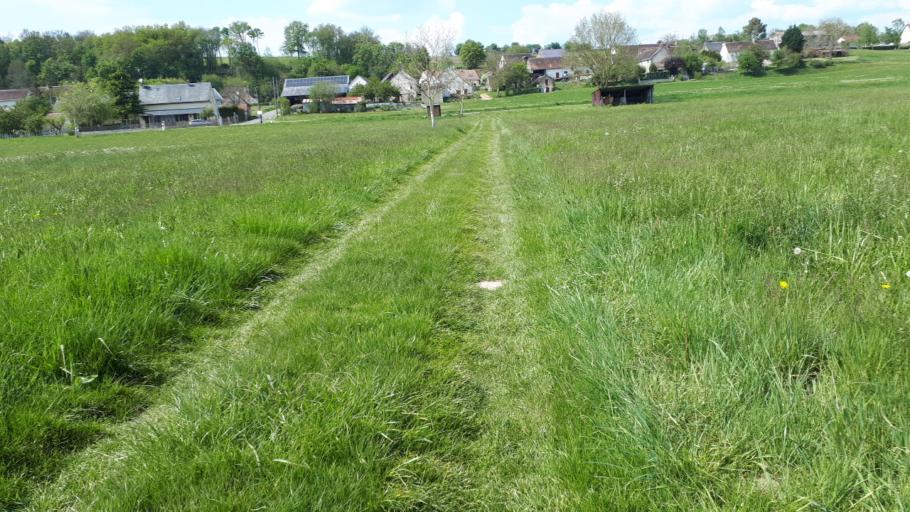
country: FR
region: Centre
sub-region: Departement du Loir-et-Cher
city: Villiers-sur-Loir
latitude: 47.8285
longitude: 0.9786
